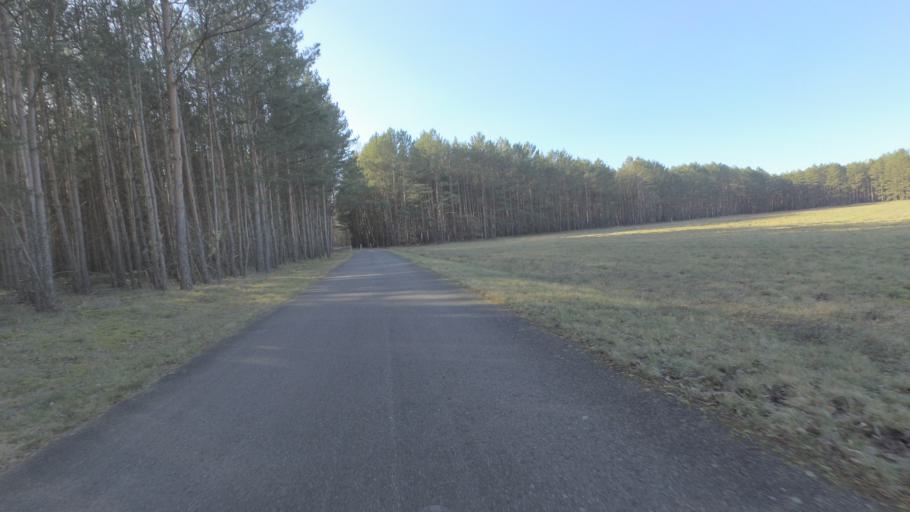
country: DE
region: Brandenburg
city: Luckenwalde
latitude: 52.0551
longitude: 13.1533
